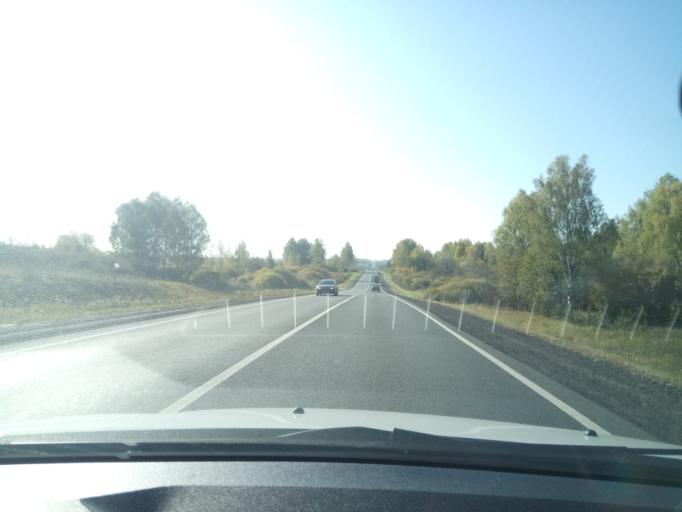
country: RU
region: Nizjnij Novgorod
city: Dal'neye Konstantinovo
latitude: 55.9706
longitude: 43.9735
